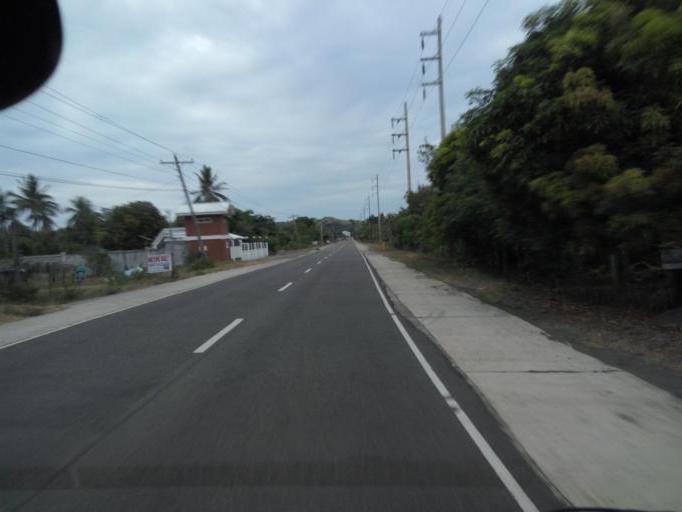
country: PH
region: Cagayan Valley
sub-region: Province of Cagayan
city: Casambalangan
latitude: 18.4019
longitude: 122.1261
